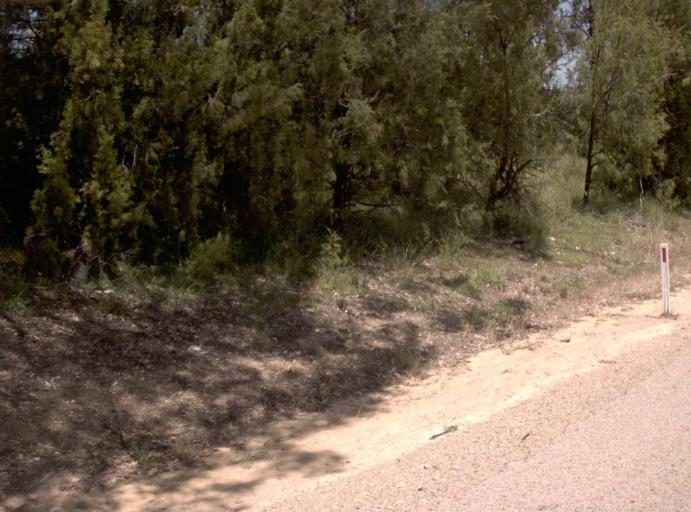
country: AU
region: Victoria
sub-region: East Gippsland
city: Bairnsdale
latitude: -37.7561
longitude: 147.7116
